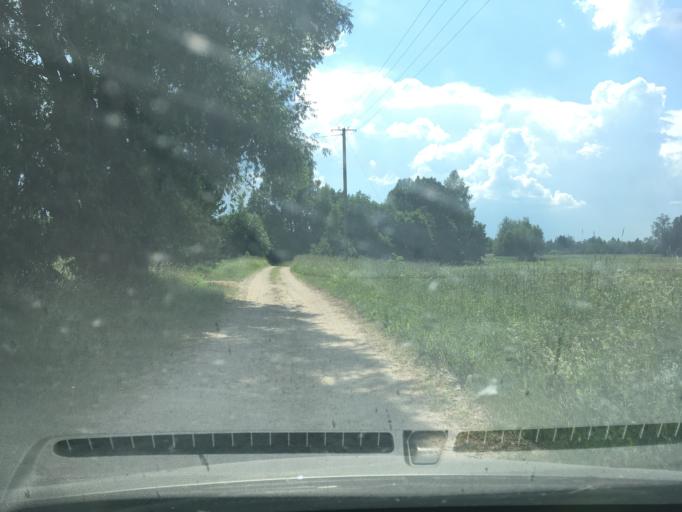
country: EE
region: Raplamaa
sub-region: Maerjamaa vald
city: Marjamaa
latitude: 58.8085
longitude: 24.4599
